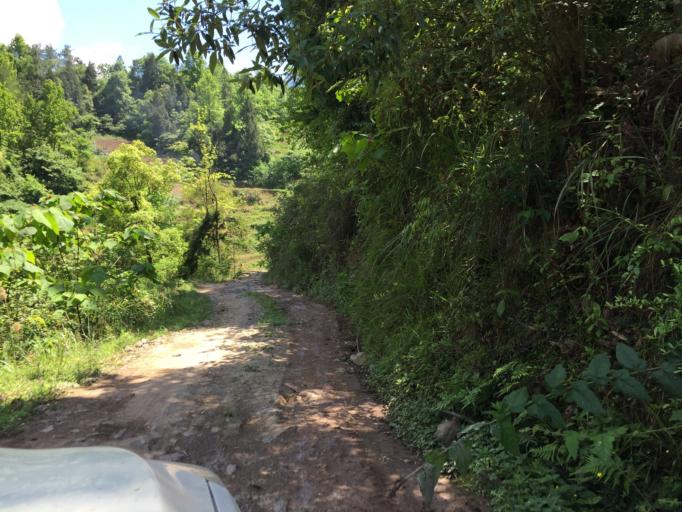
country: CN
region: Guizhou Sheng
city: Xujiaba
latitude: 27.6760
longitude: 108.0816
